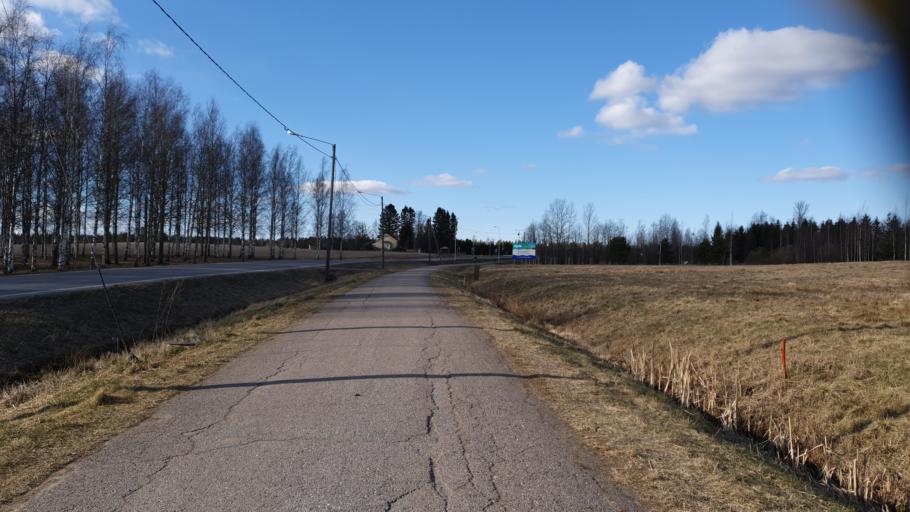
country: FI
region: Uusimaa
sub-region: Helsinki
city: Tuusula
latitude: 60.3900
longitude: 24.9886
